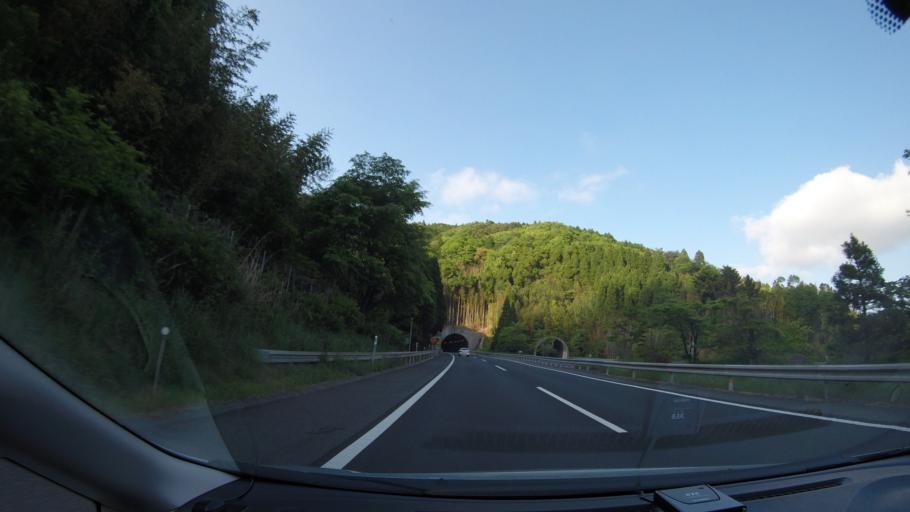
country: JP
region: Oita
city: Beppu
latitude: 33.2675
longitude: 131.3391
